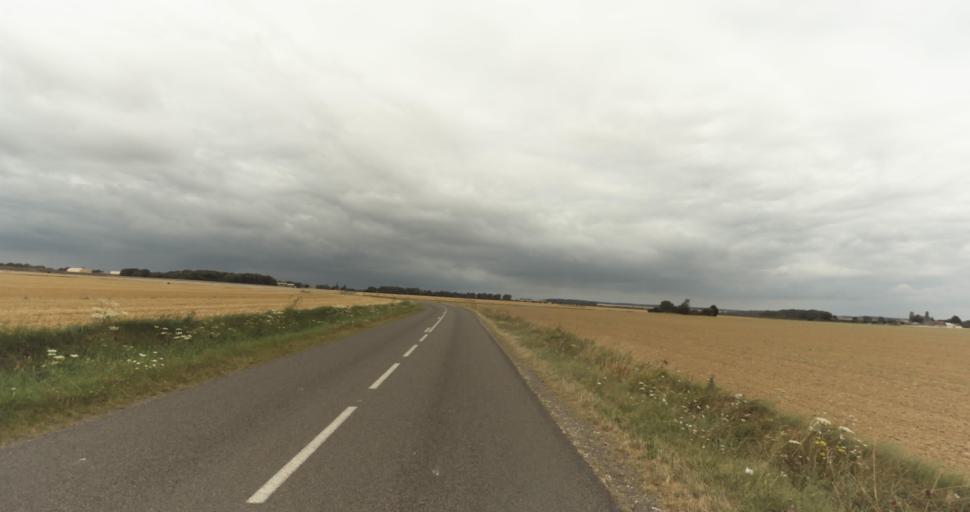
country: FR
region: Haute-Normandie
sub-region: Departement de l'Eure
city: Gravigny
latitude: 49.0383
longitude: 1.2388
